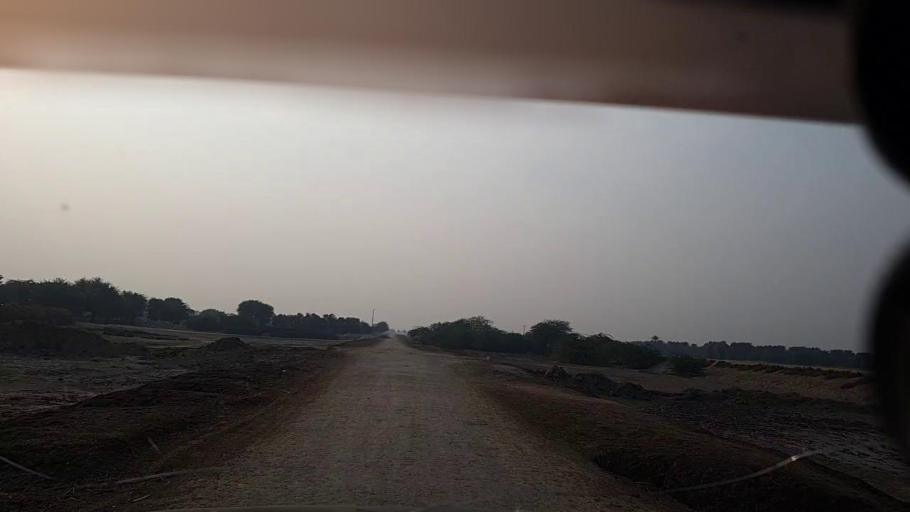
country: PK
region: Sindh
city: Gambat
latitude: 27.4355
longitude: 68.6098
